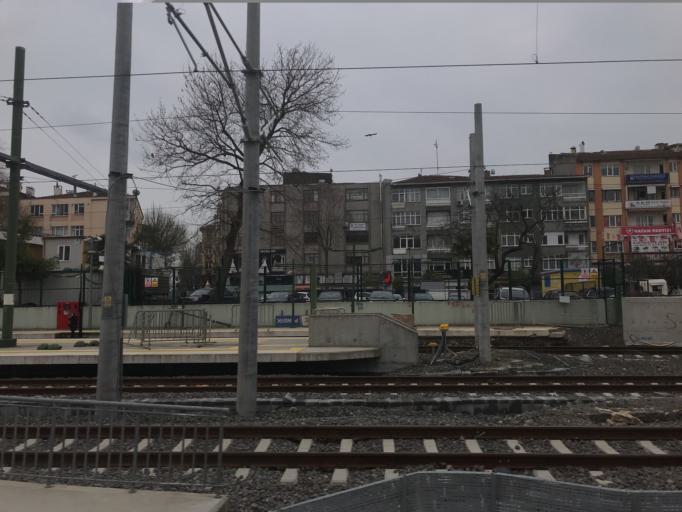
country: TR
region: Istanbul
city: Pendik
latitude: 40.8798
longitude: 29.2303
